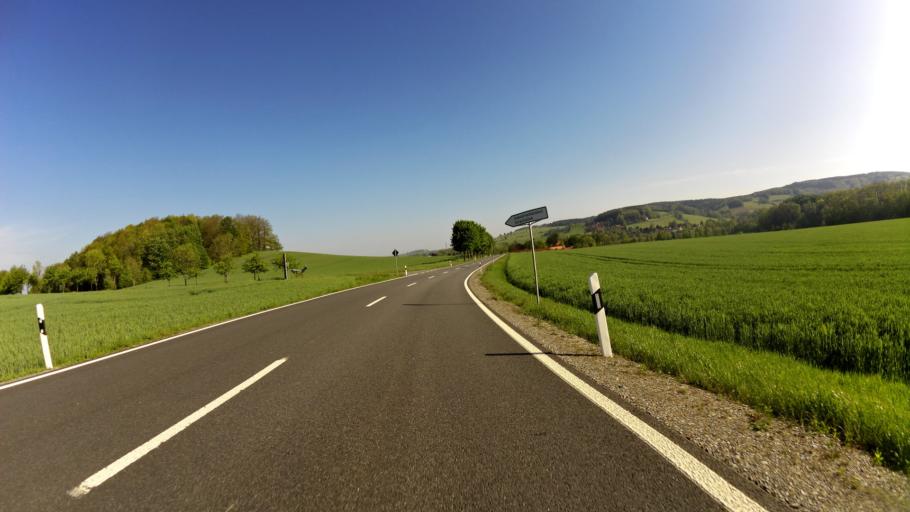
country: DE
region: Saxony
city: Neustadt in Sachsen
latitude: 51.0161
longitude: 14.2321
